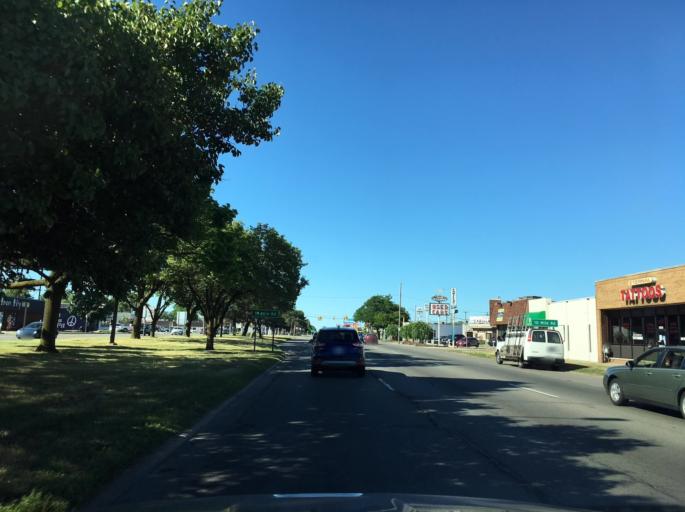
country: US
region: Michigan
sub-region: Macomb County
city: Eastpointe
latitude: 42.4783
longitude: -82.9489
